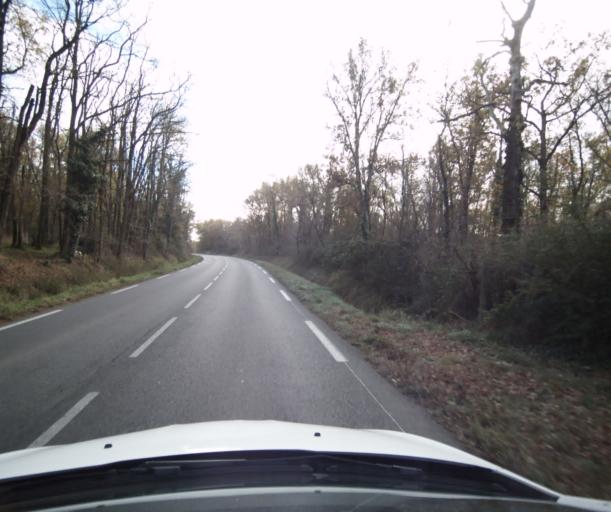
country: FR
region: Midi-Pyrenees
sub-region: Departement de la Haute-Garonne
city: Saint-Sauveur
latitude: 43.7420
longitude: 1.4088
